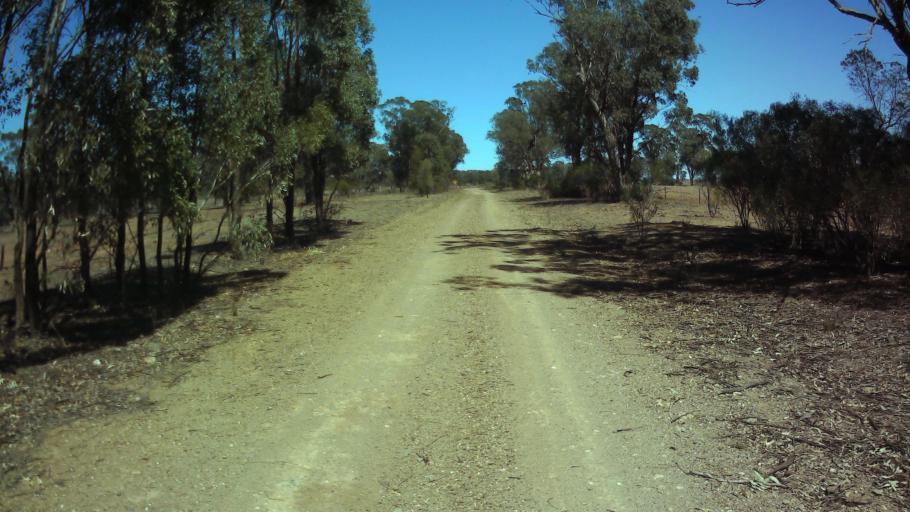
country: AU
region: New South Wales
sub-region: Forbes
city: Forbes
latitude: -33.6977
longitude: 147.8513
